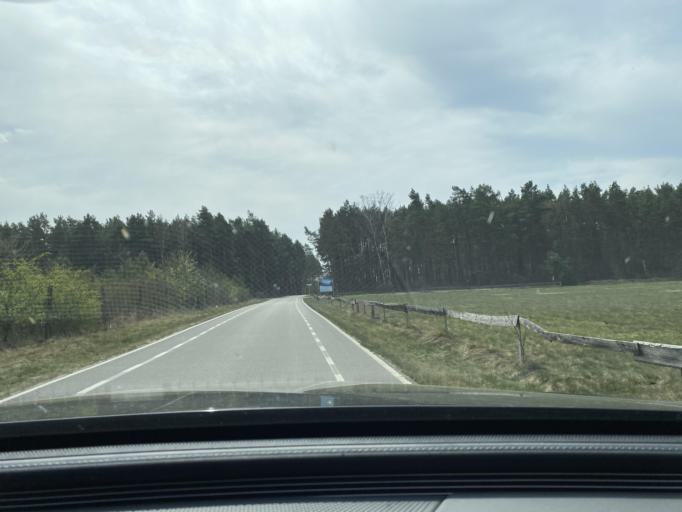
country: DE
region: Brandenburg
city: Welzow
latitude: 51.4960
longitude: 14.1344
